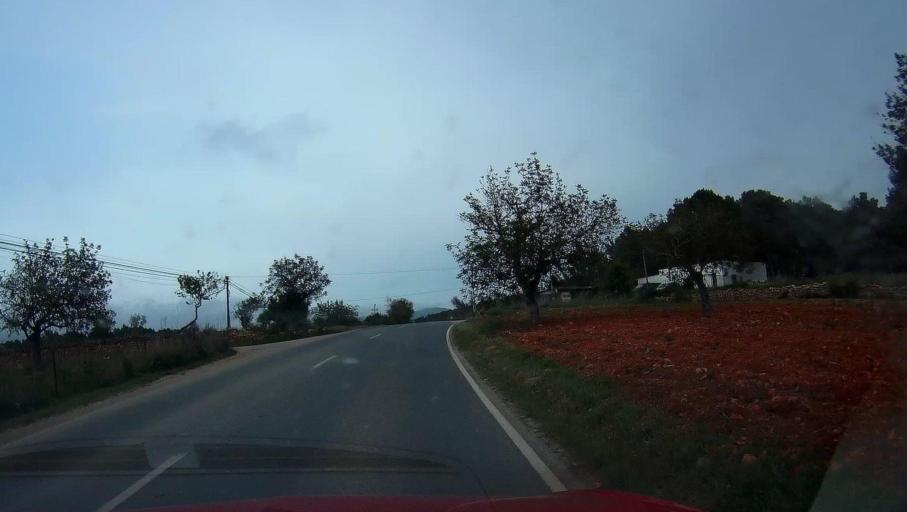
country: ES
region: Balearic Islands
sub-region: Illes Balears
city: Sant Joan de Labritja
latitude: 39.0562
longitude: 1.4517
